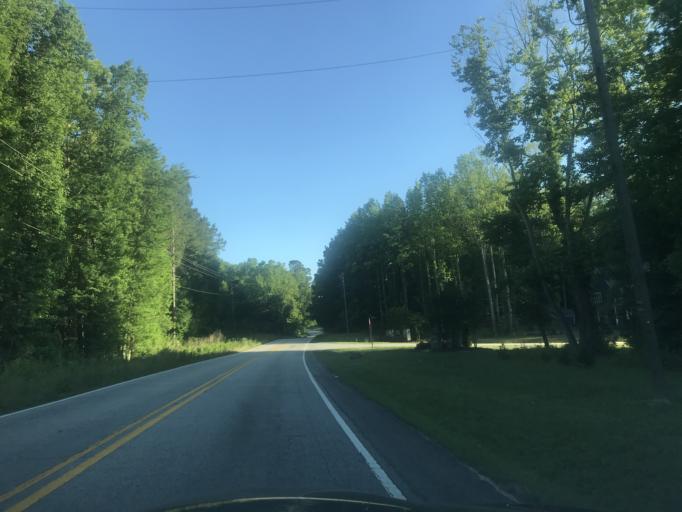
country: US
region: North Carolina
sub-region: Johnston County
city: Archer Lodge
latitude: 35.7184
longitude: -78.3840
